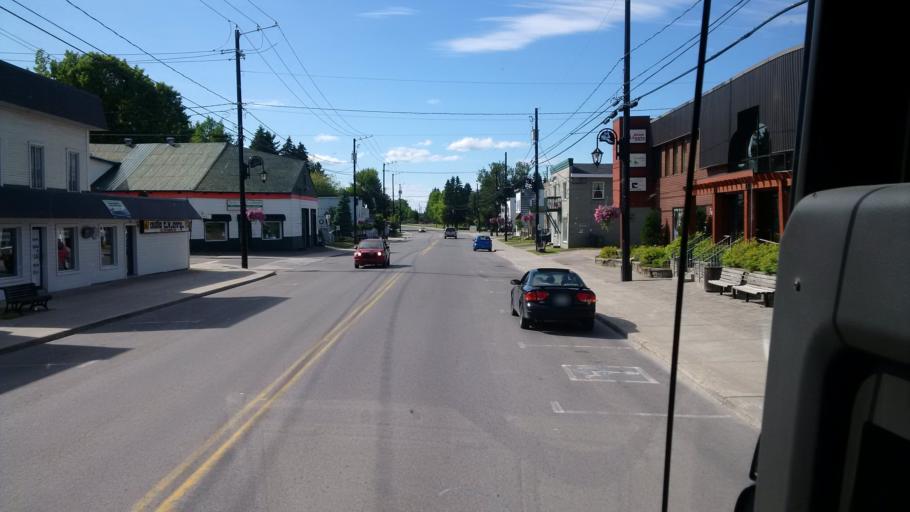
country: CA
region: Quebec
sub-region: Laurentides
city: Riviere-Rouge
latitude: 46.4153
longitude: -74.8722
